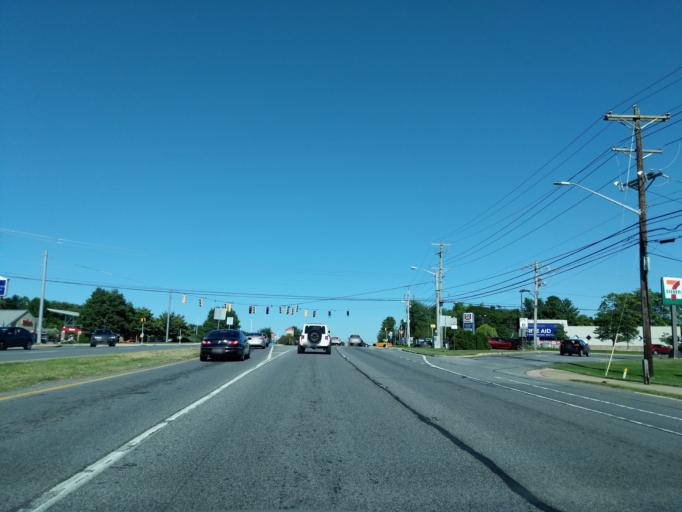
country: US
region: Delaware
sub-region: New Castle County
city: Bear
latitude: 39.6180
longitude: -75.6961
